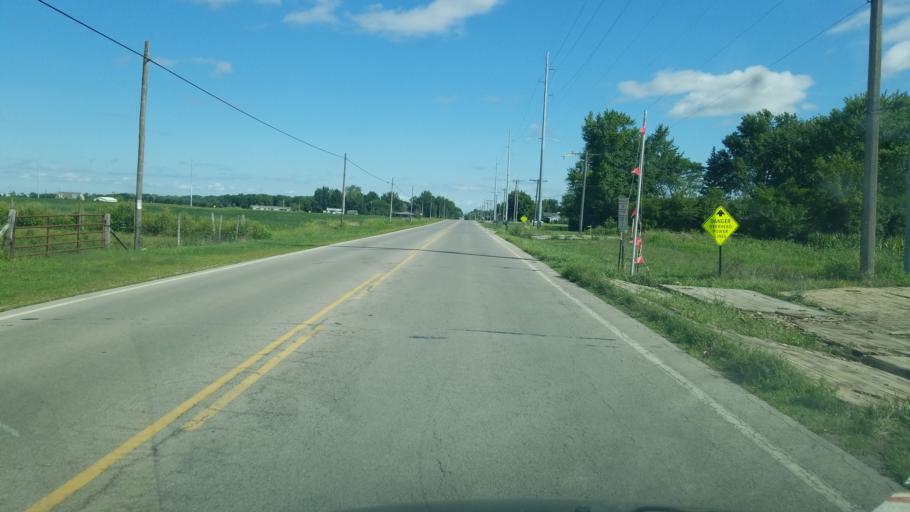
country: US
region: Ohio
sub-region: Wood County
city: North Baltimore
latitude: 41.1195
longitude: -83.6496
